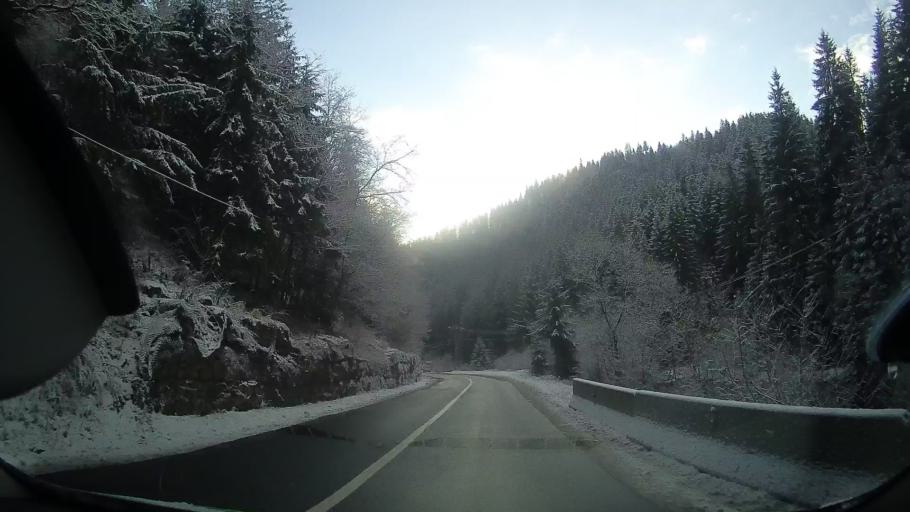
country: RO
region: Alba
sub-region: Comuna Scarisoara
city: Scarisoara
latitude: 46.4551
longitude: 22.8563
